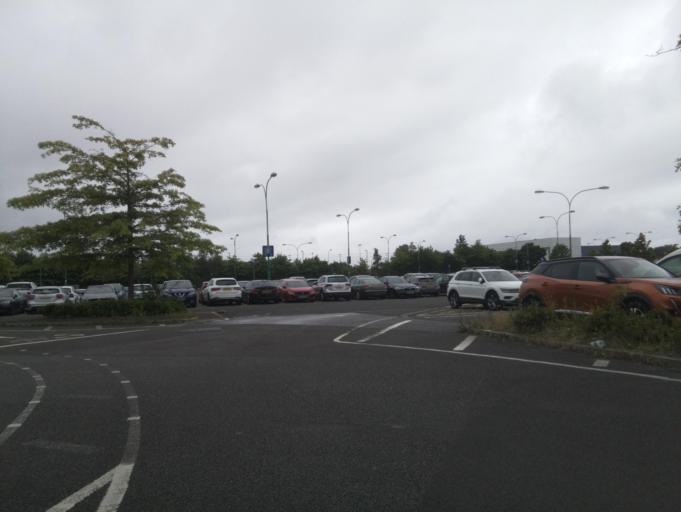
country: GB
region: England
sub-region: West Sussex
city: Langley Green
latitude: 51.1581
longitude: -0.1950
